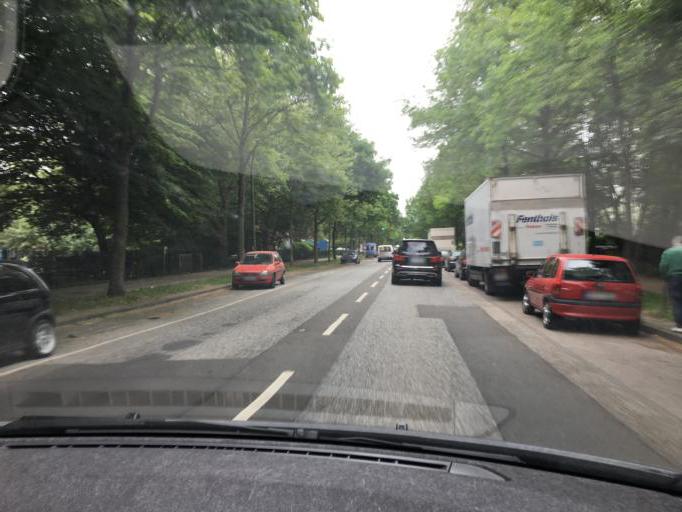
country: DE
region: Hamburg
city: Kleiner Grasbrook
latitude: 53.5108
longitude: 9.9928
